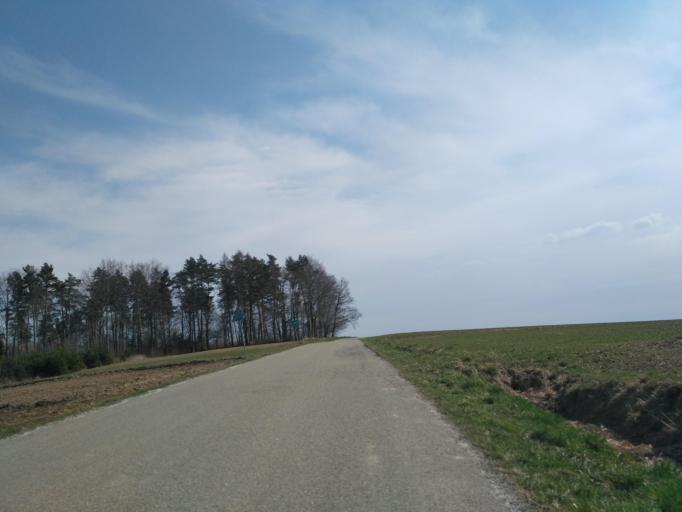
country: PL
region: Subcarpathian Voivodeship
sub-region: Powiat ropczycko-sedziszowski
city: Iwierzyce
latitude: 49.9722
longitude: 21.7539
